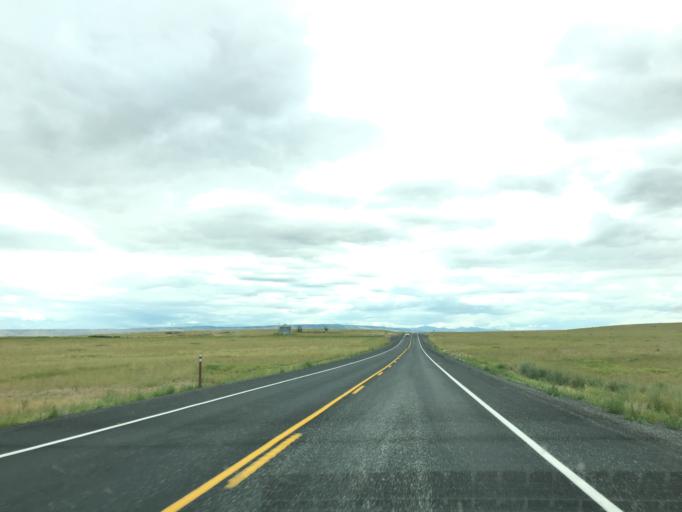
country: US
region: Washington
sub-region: Douglas County
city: Waterville
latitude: 47.6127
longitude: -119.8304
